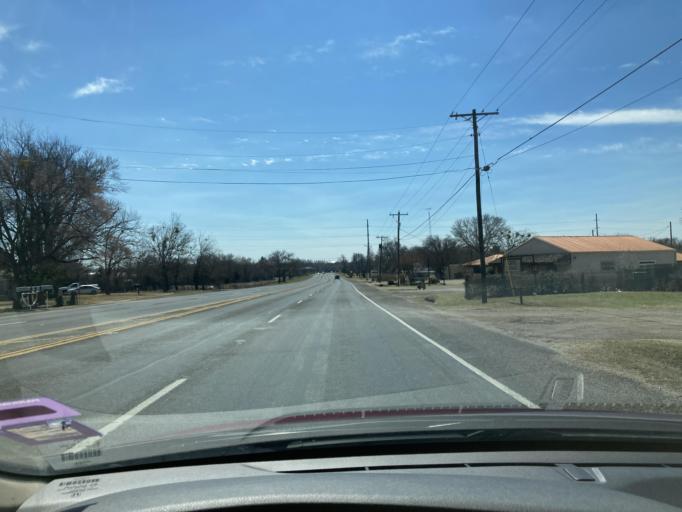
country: US
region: Texas
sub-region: Navarro County
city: Corsicana
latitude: 32.1134
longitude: -96.4644
